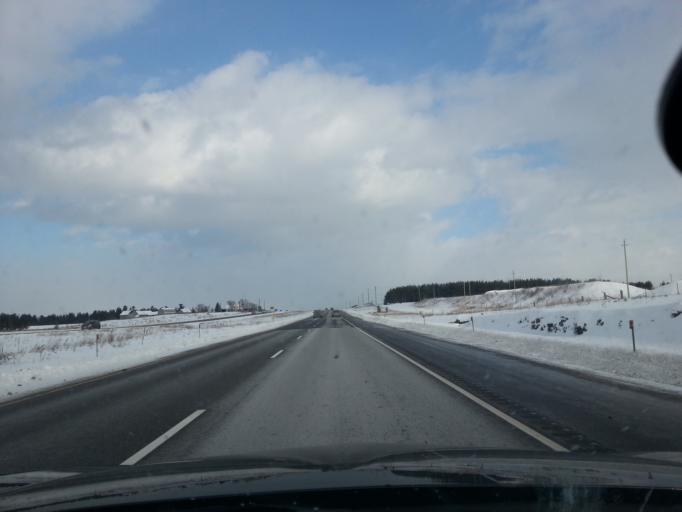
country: CA
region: Ontario
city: Carleton Place
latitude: 45.2298
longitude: -75.9950
